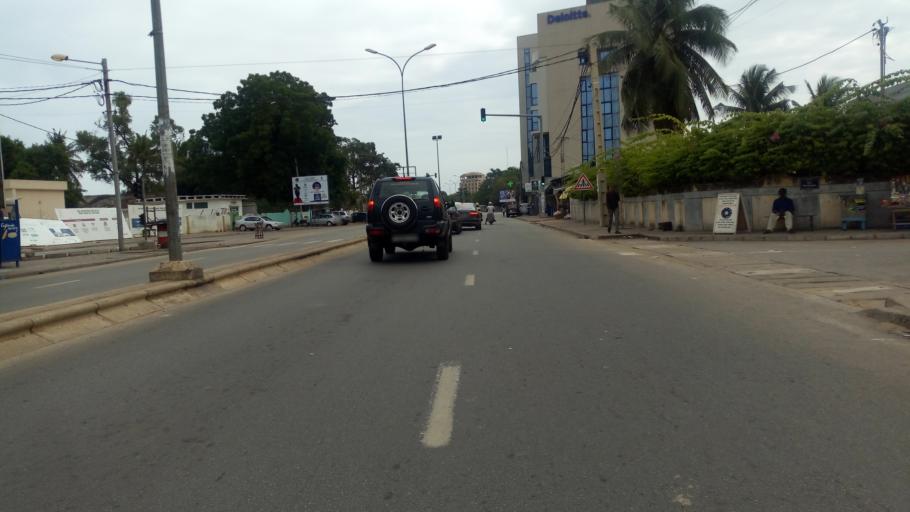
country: TG
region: Maritime
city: Lome
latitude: 6.1294
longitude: 1.2112
